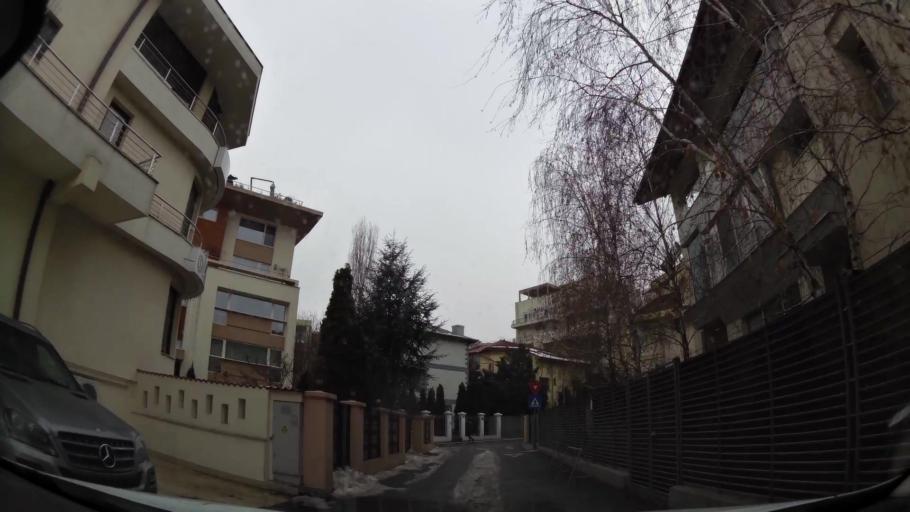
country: RO
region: Bucuresti
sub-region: Municipiul Bucuresti
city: Bucharest
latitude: 44.4826
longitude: 26.0874
